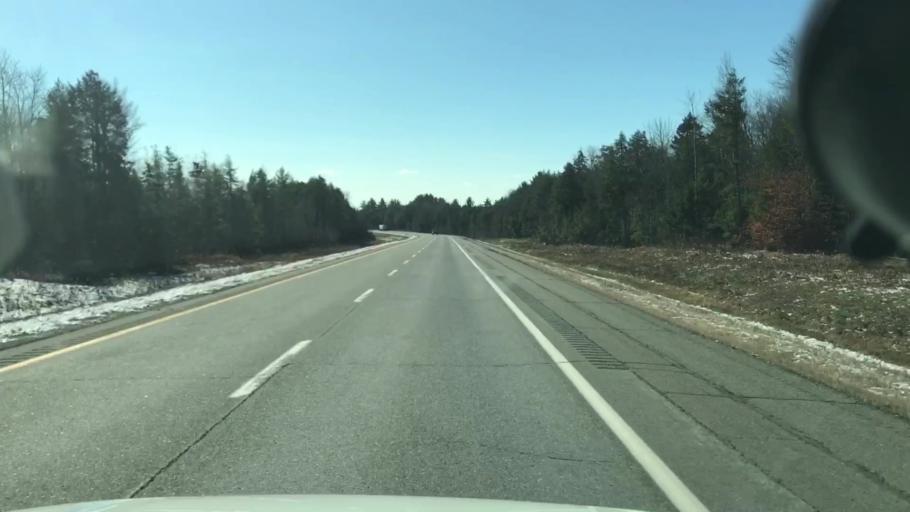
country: US
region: Maine
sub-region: Penobscot County
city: Howland
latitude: 45.2754
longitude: -68.6761
